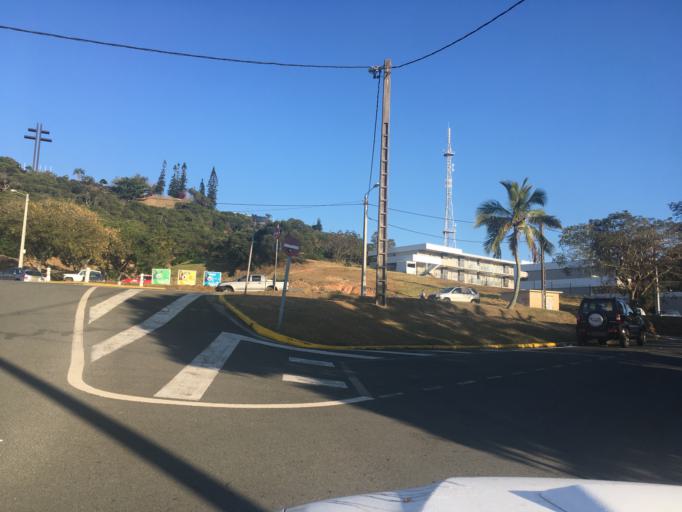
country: NC
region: South Province
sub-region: Noumea
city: Noumea
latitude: -22.2794
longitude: 166.4491
